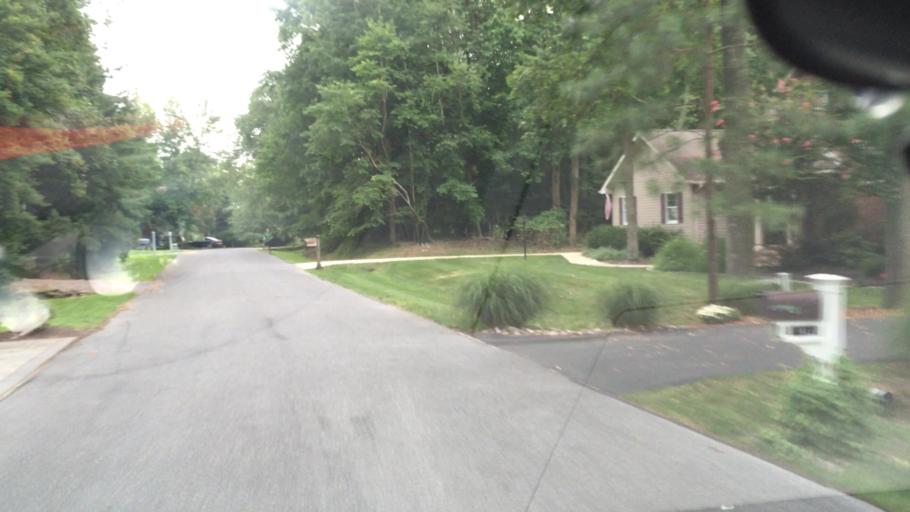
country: US
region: Delaware
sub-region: Sussex County
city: Rehoboth Beach
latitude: 38.6979
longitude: -75.0856
